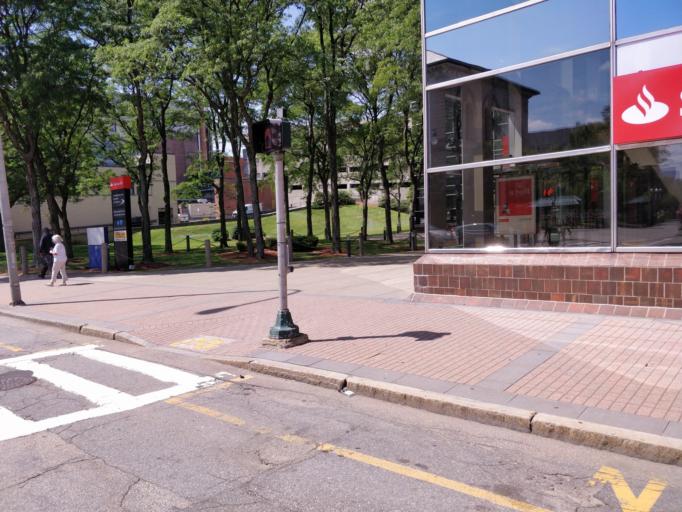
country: US
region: Massachusetts
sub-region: Worcester County
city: Worcester
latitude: 42.2633
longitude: -71.8023
